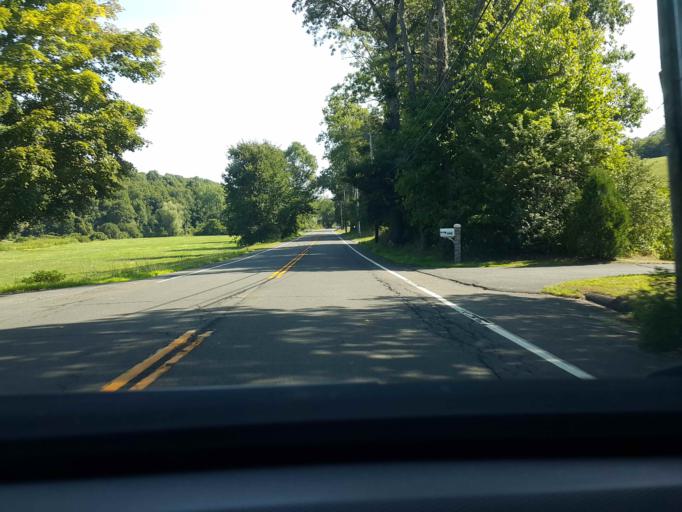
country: US
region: Connecticut
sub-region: Middlesex County
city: Durham
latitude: 41.4431
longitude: -72.6879
